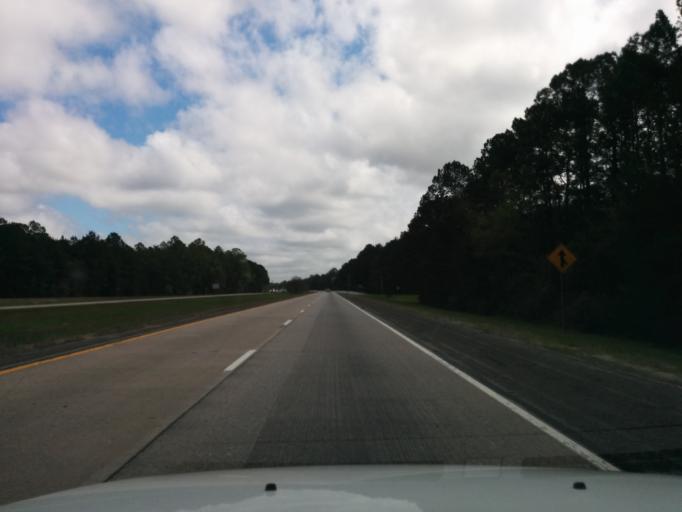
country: US
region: Georgia
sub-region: Chatham County
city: Bloomingdale
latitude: 32.1239
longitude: -81.3860
